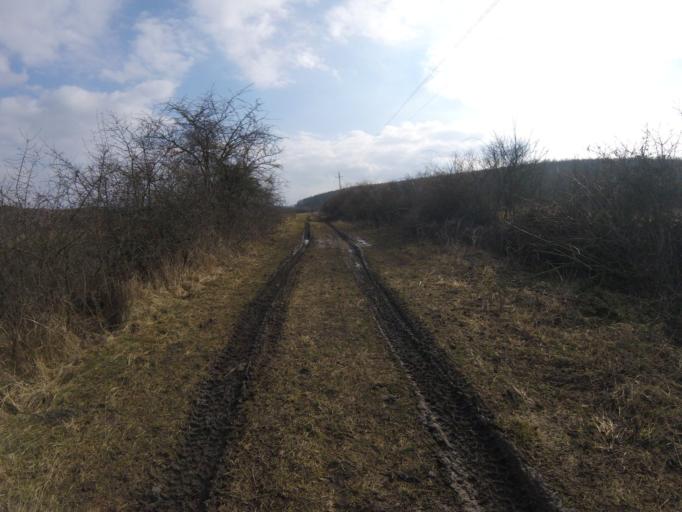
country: HU
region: Heves
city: Egerszalok
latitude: 47.8516
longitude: 20.3225
